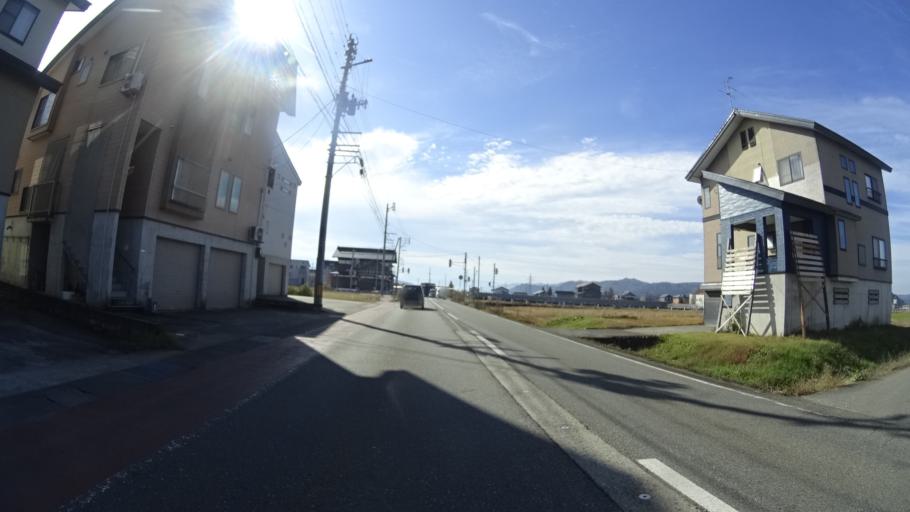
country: JP
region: Niigata
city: Ojiya
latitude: 37.2353
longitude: 138.9766
